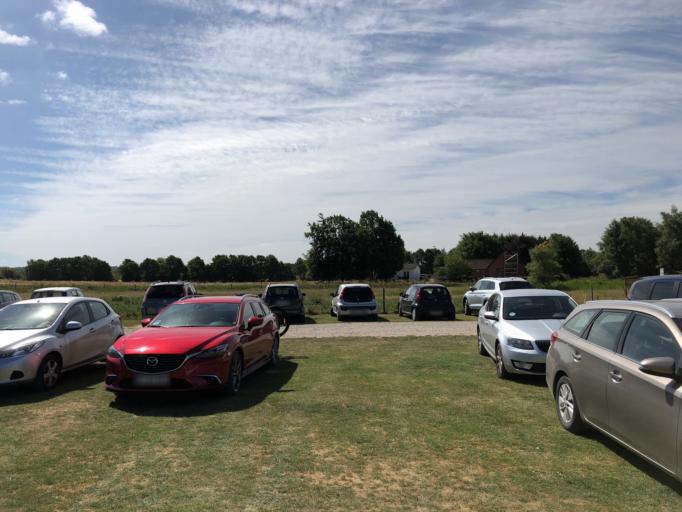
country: DK
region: North Denmark
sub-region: Mariagerfjord Kommune
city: Hobro
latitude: 56.5899
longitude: 9.6395
